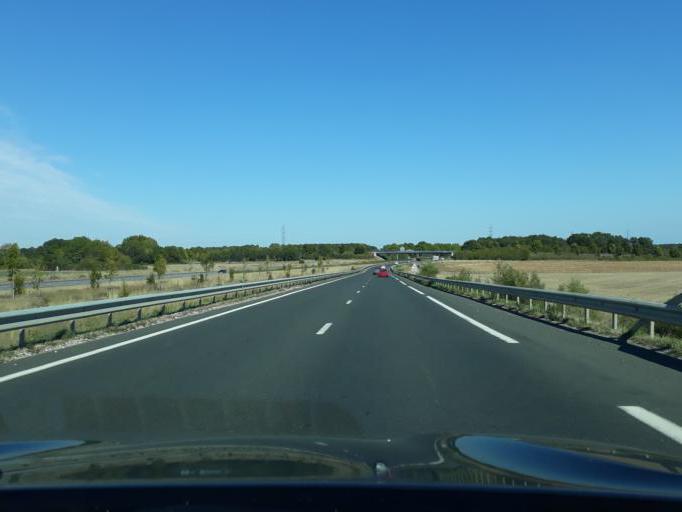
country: FR
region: Centre
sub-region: Departement d'Indre-et-Loire
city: Artannes-sur-Indre
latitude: 47.3053
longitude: 0.5674
